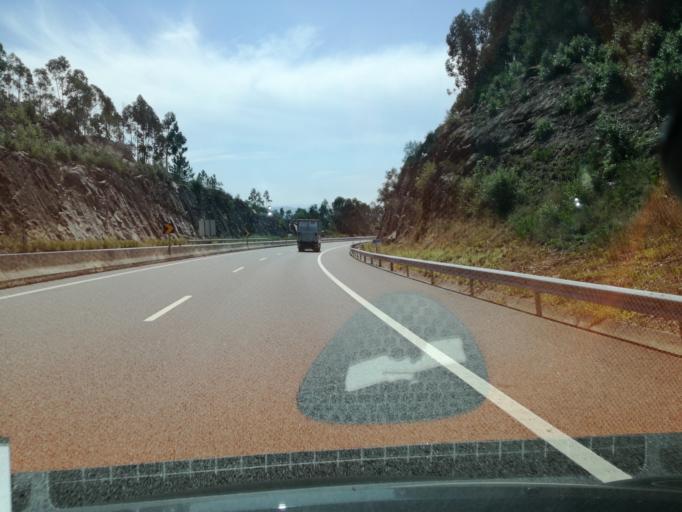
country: PT
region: Viana do Castelo
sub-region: Viana do Castelo
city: Meadela
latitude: 41.7406
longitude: -8.7923
